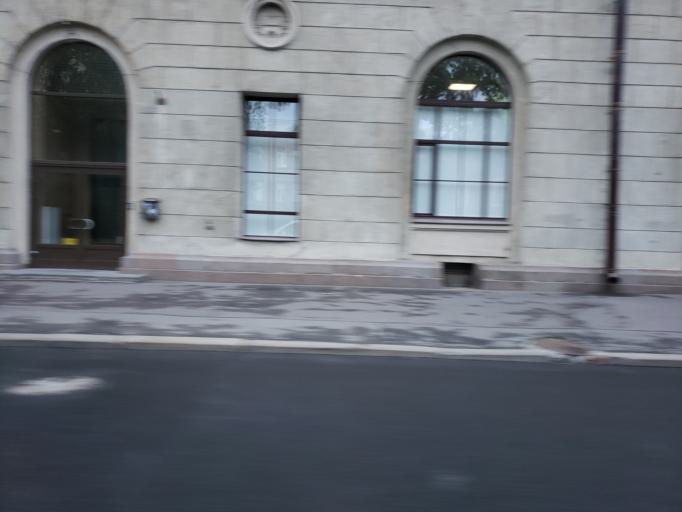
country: RU
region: St.-Petersburg
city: Vasyl'evsky Ostrov
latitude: 59.9308
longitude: 30.2546
